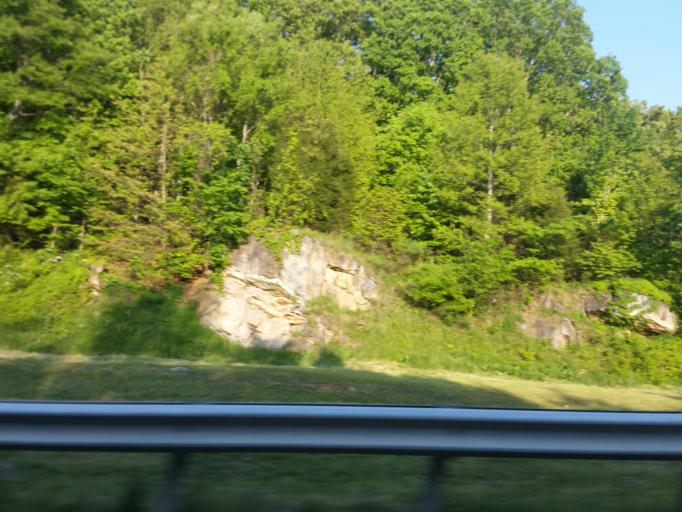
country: US
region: Virginia
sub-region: Russell County
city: Lebanon
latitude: 36.8746
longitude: -82.1102
